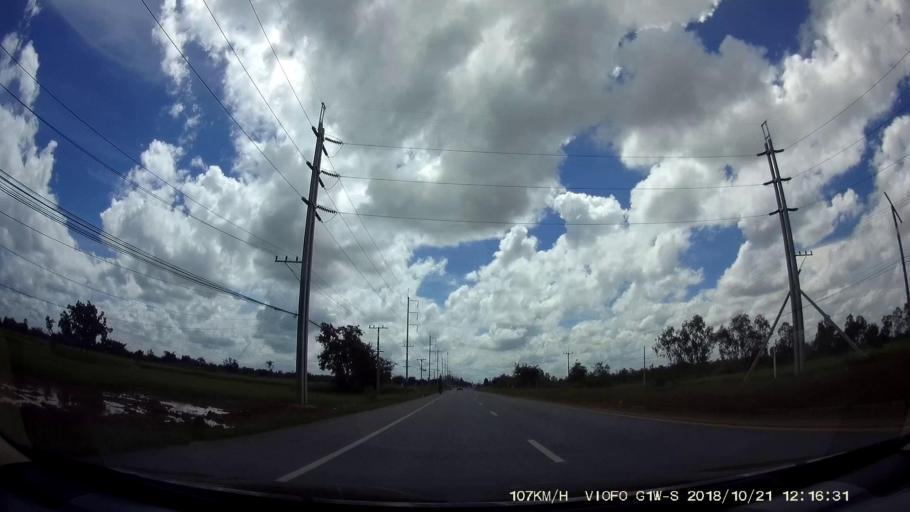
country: TH
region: Nakhon Ratchasima
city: Dan Khun Thot
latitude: 15.3462
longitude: 101.8254
